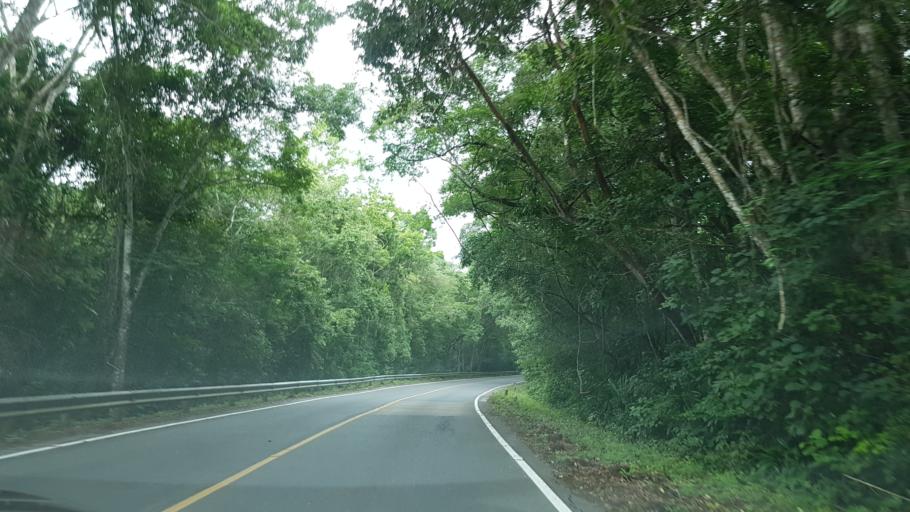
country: GT
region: Peten
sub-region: Municipio de San Jose
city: San Jose
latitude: 17.1746
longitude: -89.6414
